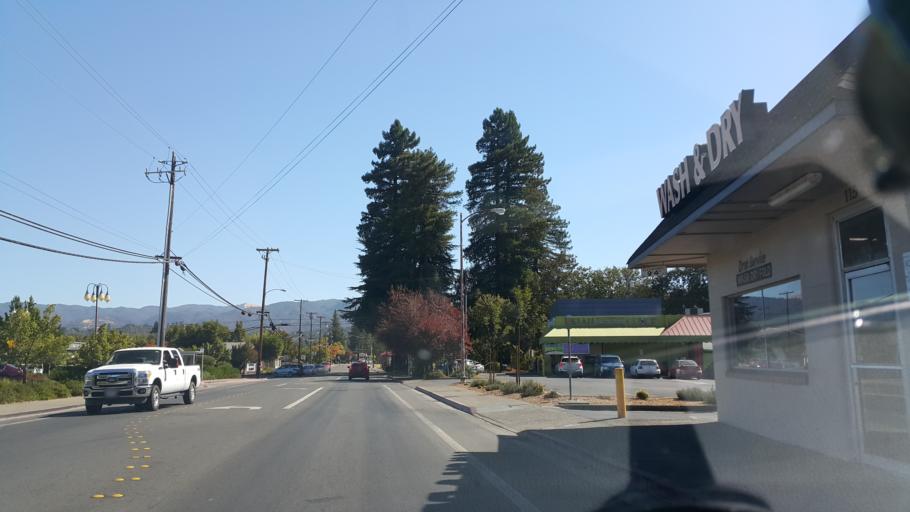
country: US
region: California
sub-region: Mendocino County
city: Ukiah
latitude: 39.1433
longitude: -123.2060
